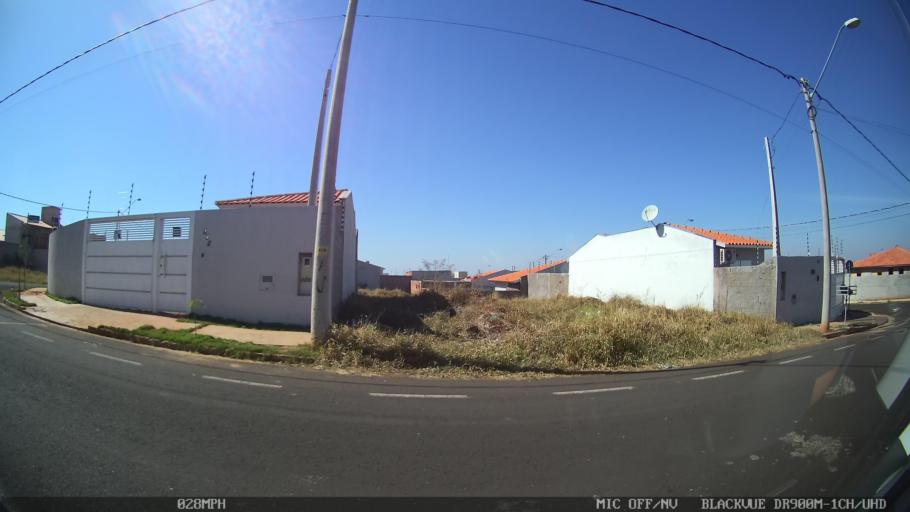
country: BR
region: Sao Paulo
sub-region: Sao Jose Do Rio Preto
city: Sao Jose do Rio Preto
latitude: -20.7595
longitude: -49.4236
